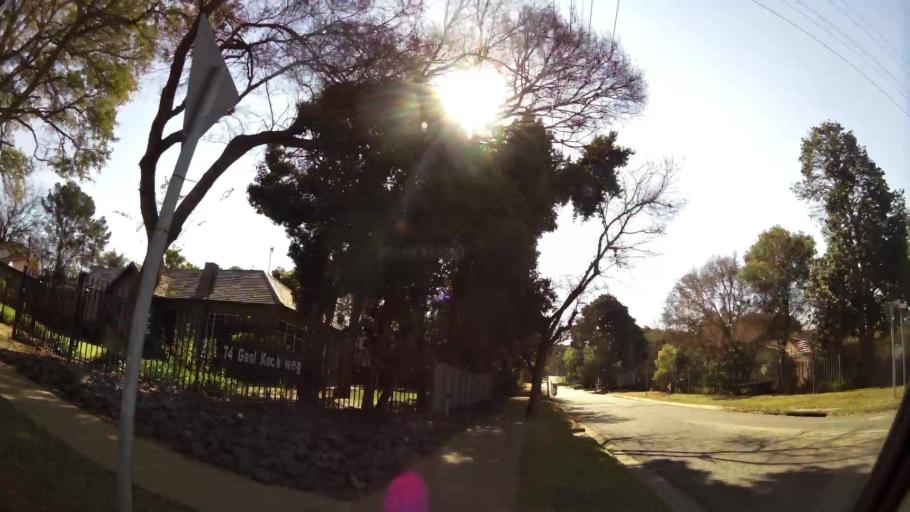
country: ZA
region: Gauteng
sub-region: City of Tshwane Metropolitan Municipality
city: Pretoria
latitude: -25.7787
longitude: 28.2632
